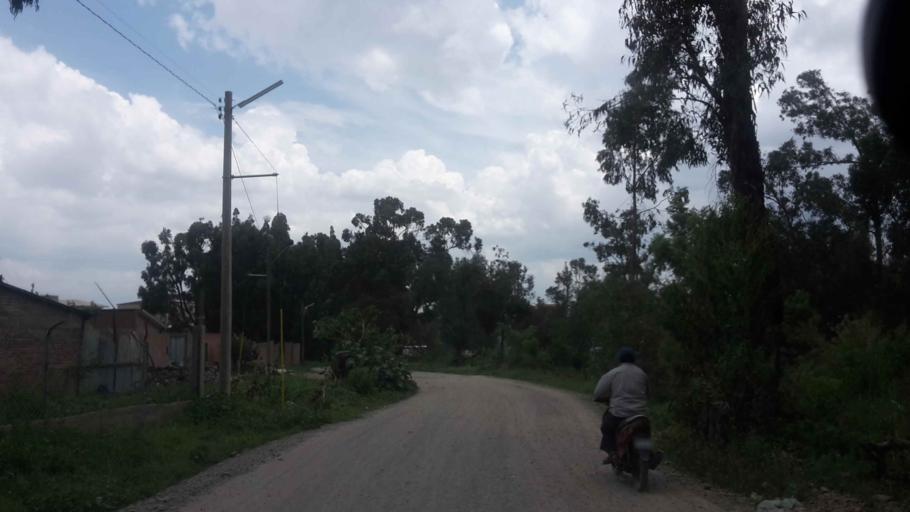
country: BO
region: Cochabamba
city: Cochabamba
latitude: -17.3341
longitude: -66.2243
